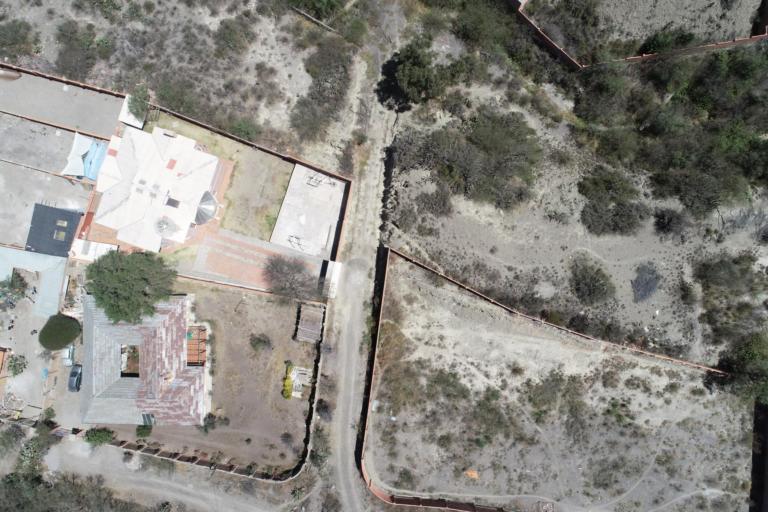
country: BO
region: La Paz
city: La Paz
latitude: -16.6251
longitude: -68.0546
